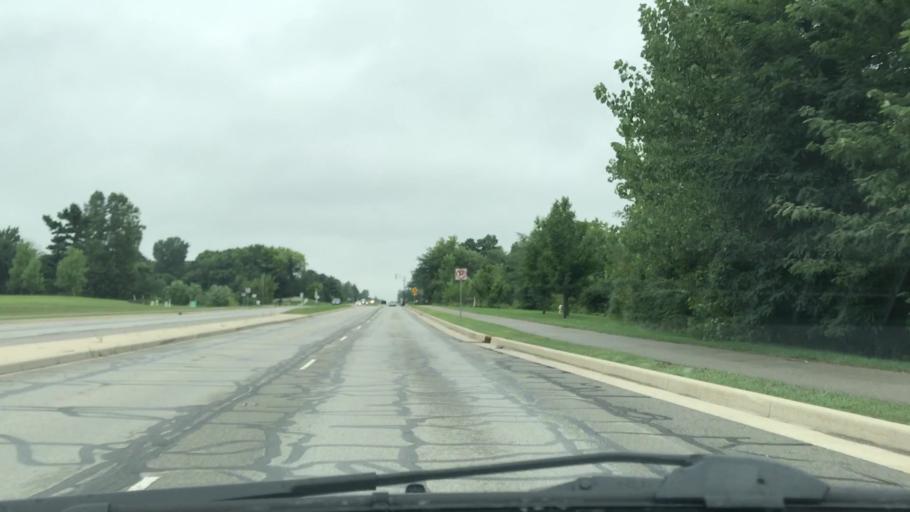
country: US
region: Indiana
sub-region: Hamilton County
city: Carmel
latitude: 40.0120
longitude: -86.0705
